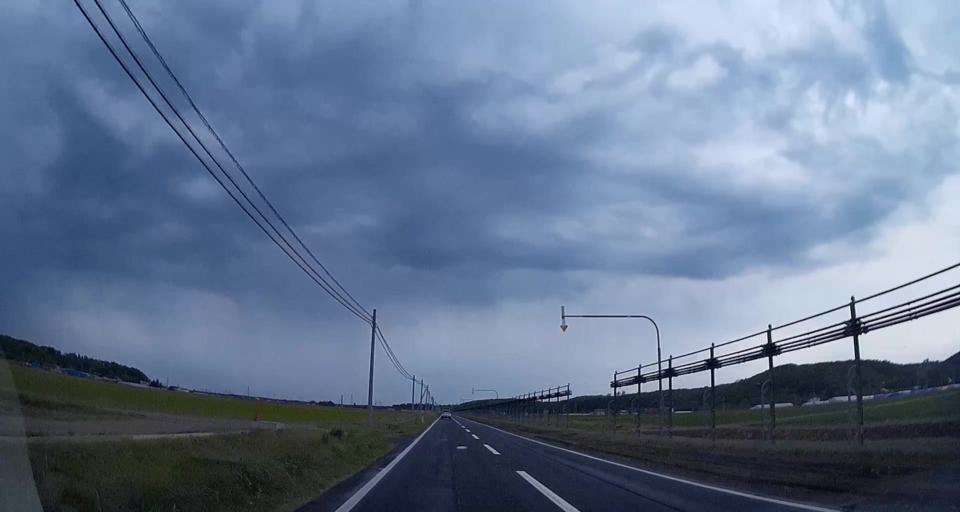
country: JP
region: Hokkaido
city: Chitose
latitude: 42.7180
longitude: 141.8679
